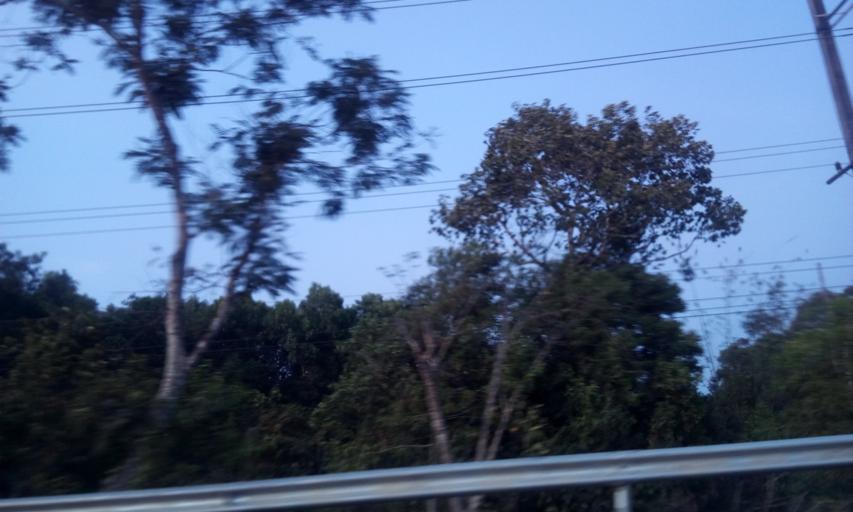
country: TH
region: Chanthaburi
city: Khlung
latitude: 12.4445
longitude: 102.2959
